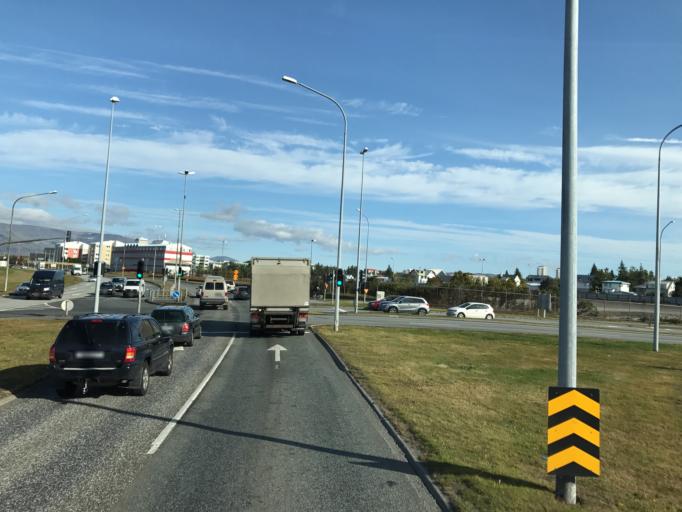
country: IS
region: Capital Region
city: Reykjavik
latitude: 64.1473
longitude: -21.8945
